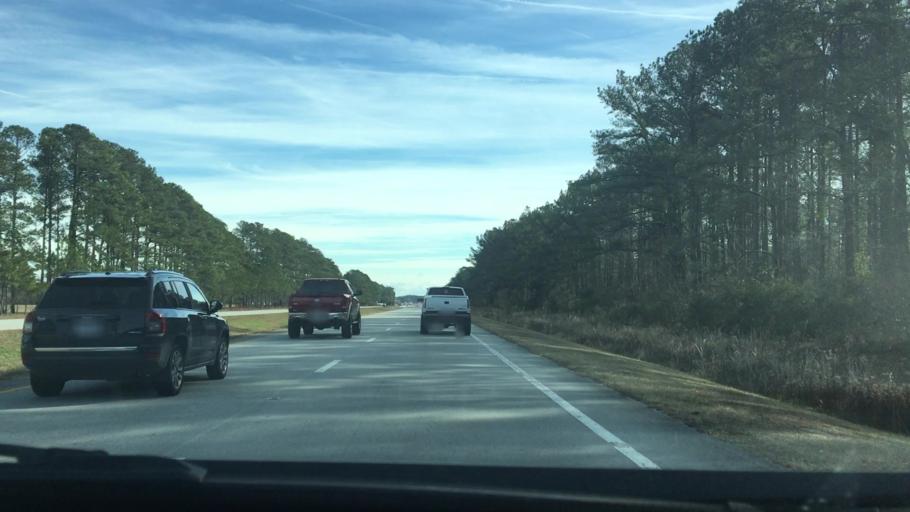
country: US
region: North Carolina
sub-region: Carteret County
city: Newport
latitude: 34.7659
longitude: -76.8596
